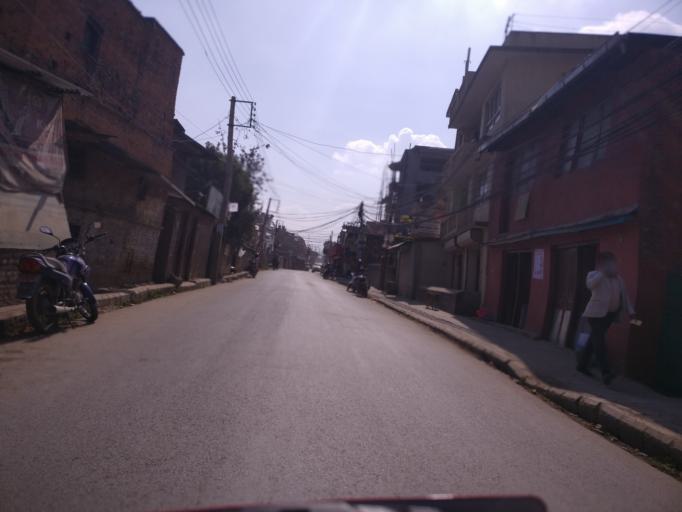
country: NP
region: Central Region
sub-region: Bagmati Zone
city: Patan
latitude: 27.6672
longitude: 85.3135
